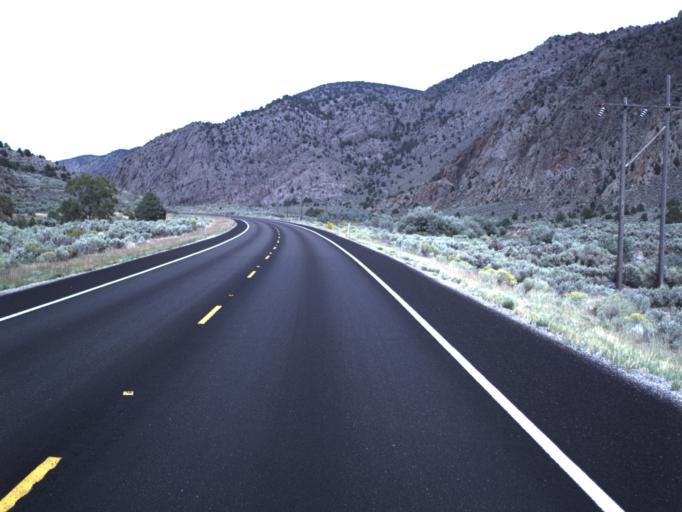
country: US
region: Utah
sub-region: Piute County
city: Junction
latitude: 38.0720
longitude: -112.3420
